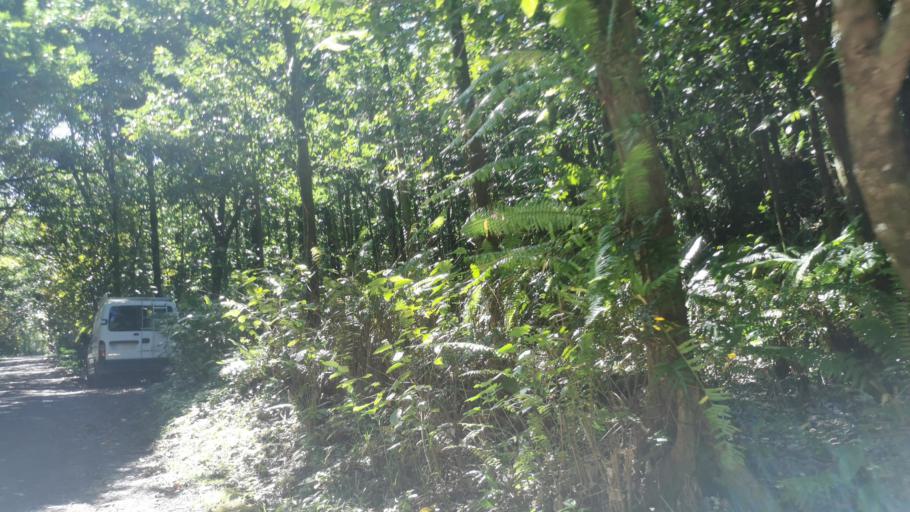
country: RE
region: Reunion
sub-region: Reunion
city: Saint-Philippe
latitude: -21.3566
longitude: 55.7404
